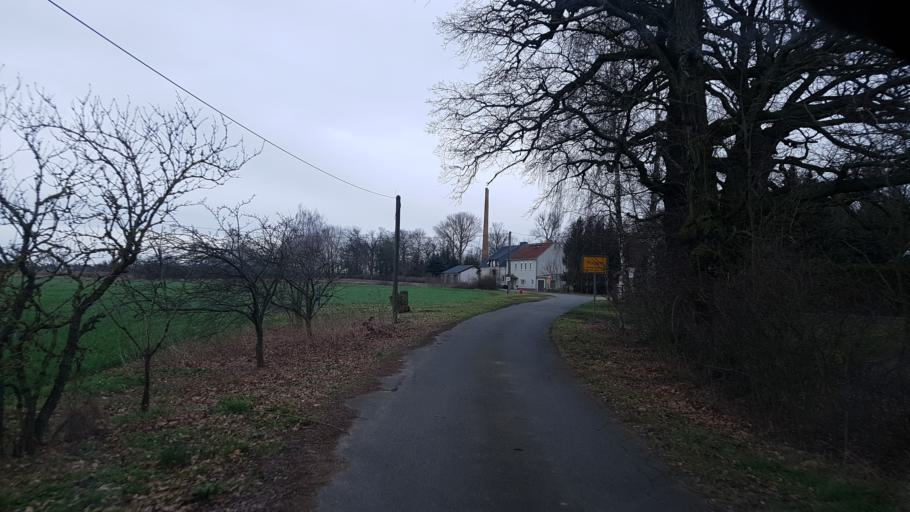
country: DE
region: Brandenburg
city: Herzberg
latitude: 51.7145
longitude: 13.2801
